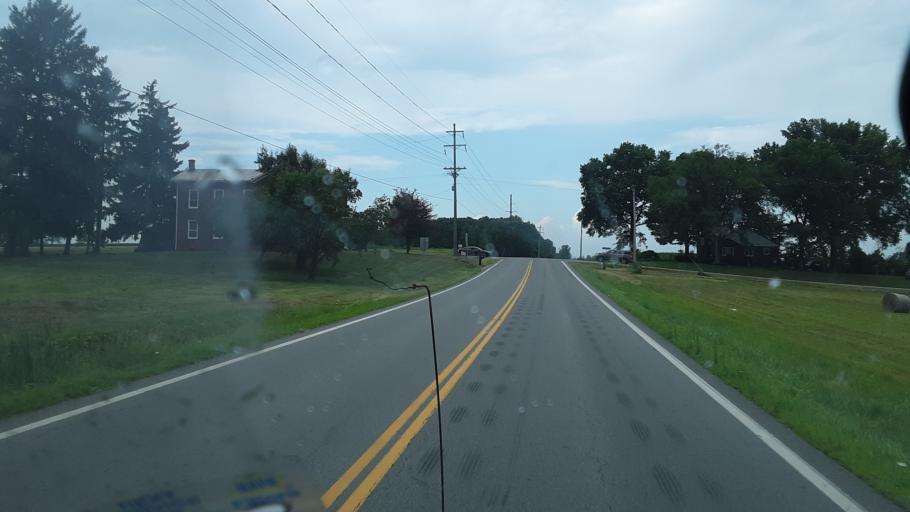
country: US
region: Ohio
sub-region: Fairfield County
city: Baltimore
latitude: 39.8107
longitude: -82.5707
